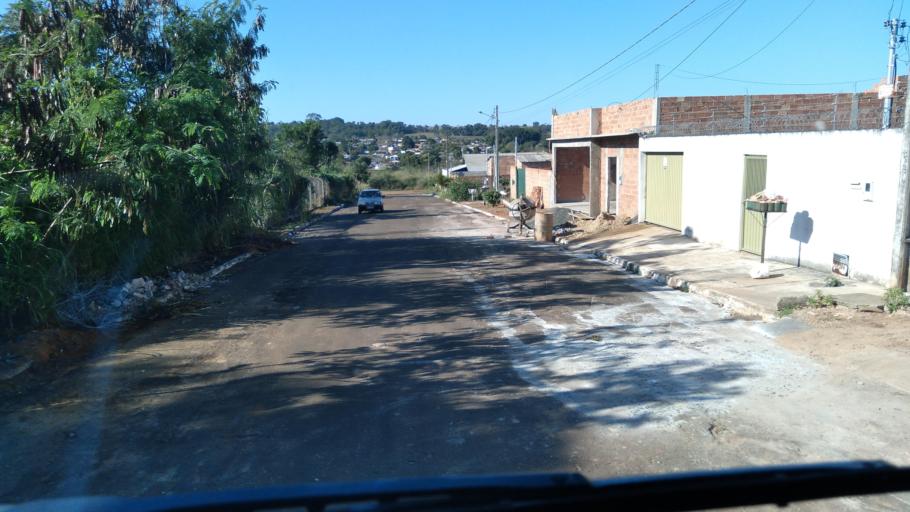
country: BR
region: Goias
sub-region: Mineiros
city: Mineiros
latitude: -17.5774
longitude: -52.5688
